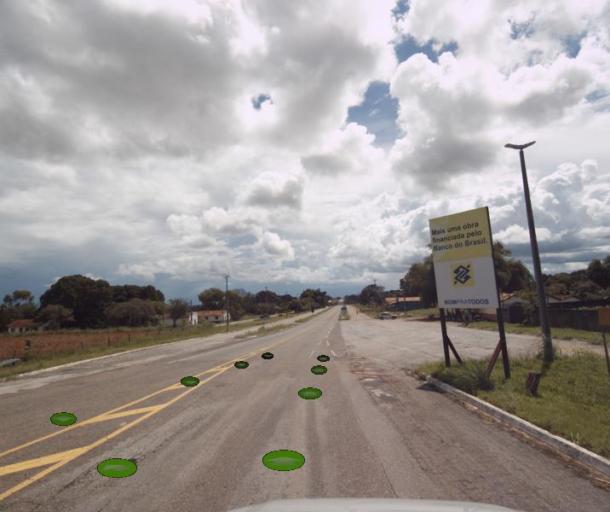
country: BR
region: Goias
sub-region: Uruacu
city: Uruacu
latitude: -14.0147
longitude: -49.0863
